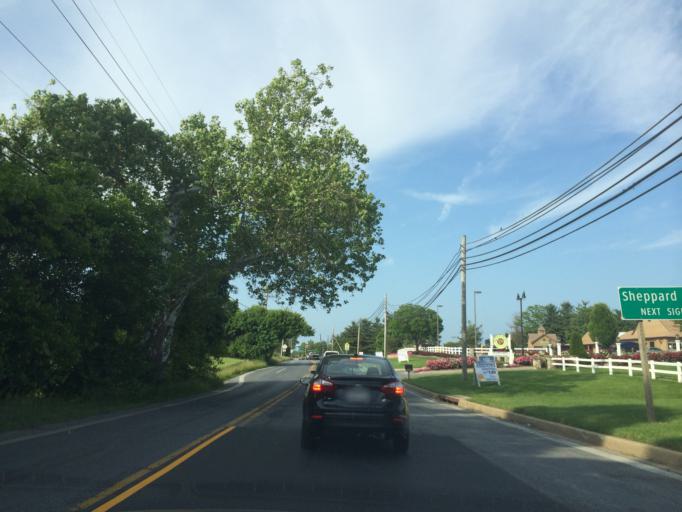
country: US
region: Maryland
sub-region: Howard County
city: Highland
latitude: 39.2146
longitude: -76.9346
